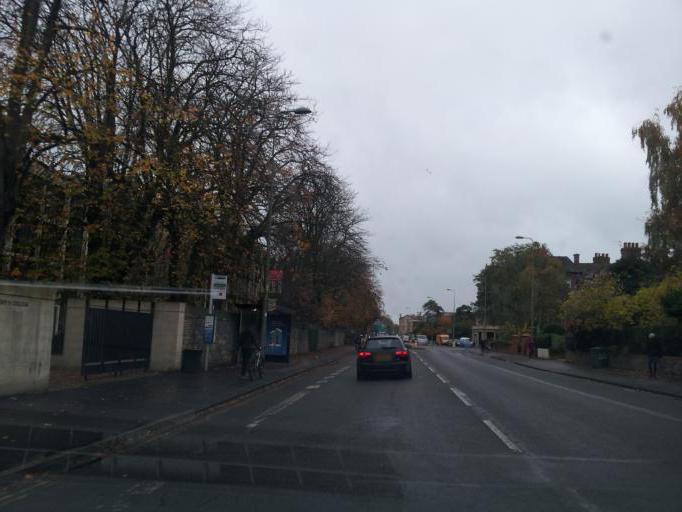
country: GB
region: England
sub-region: Oxfordshire
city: Oxford
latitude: 51.7633
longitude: -1.2637
